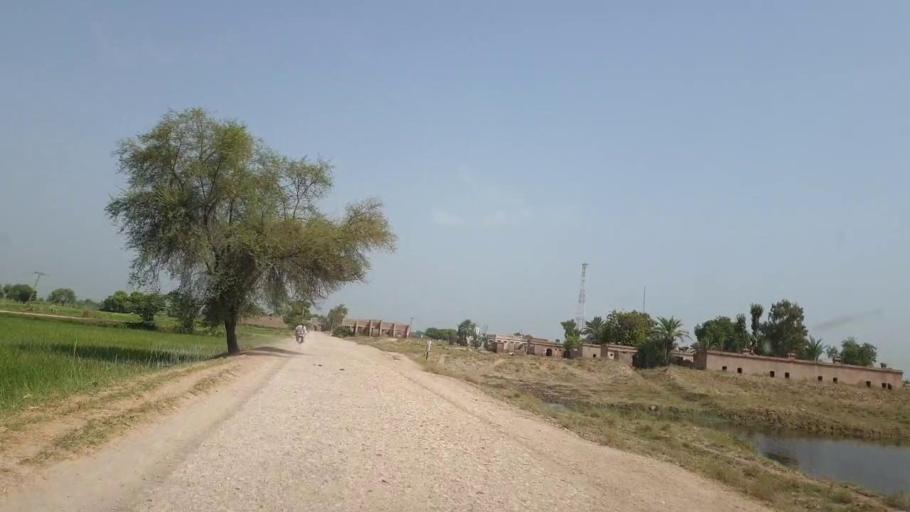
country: PK
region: Sindh
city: Lakhi
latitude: 27.8693
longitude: 68.6610
